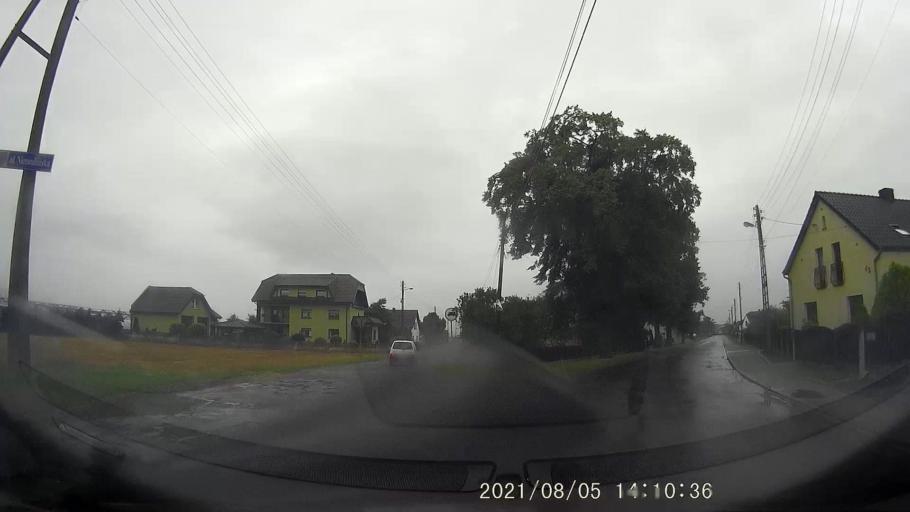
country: PL
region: Opole Voivodeship
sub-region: Powiat krapkowicki
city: Strzeleczki
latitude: 50.4717
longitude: 17.7874
